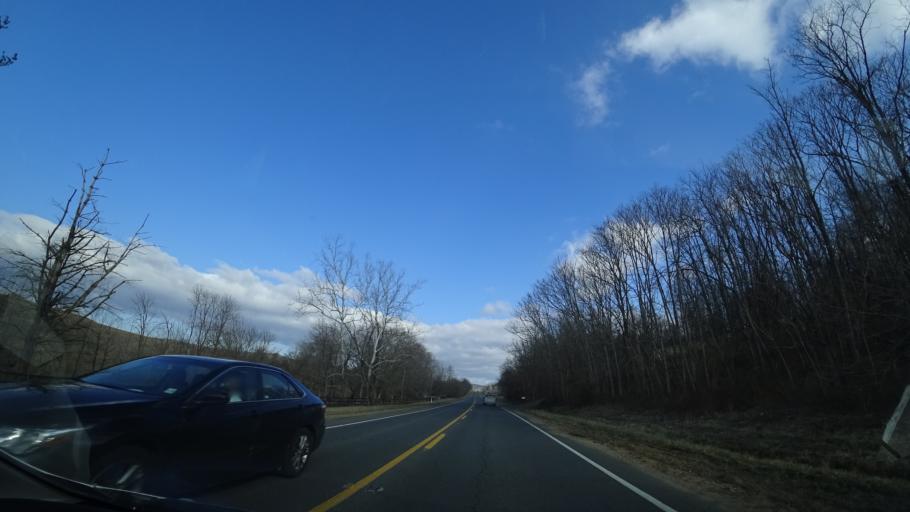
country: US
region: Virginia
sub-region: Fauquier County
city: Marshall
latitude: 38.9459
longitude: -77.9371
